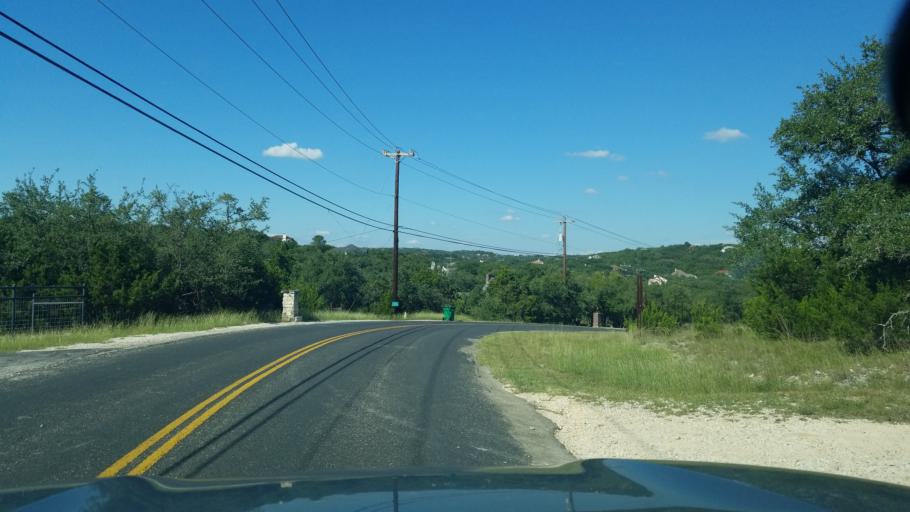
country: US
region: Texas
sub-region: Bexar County
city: Timberwood Park
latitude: 29.6787
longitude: -98.4971
